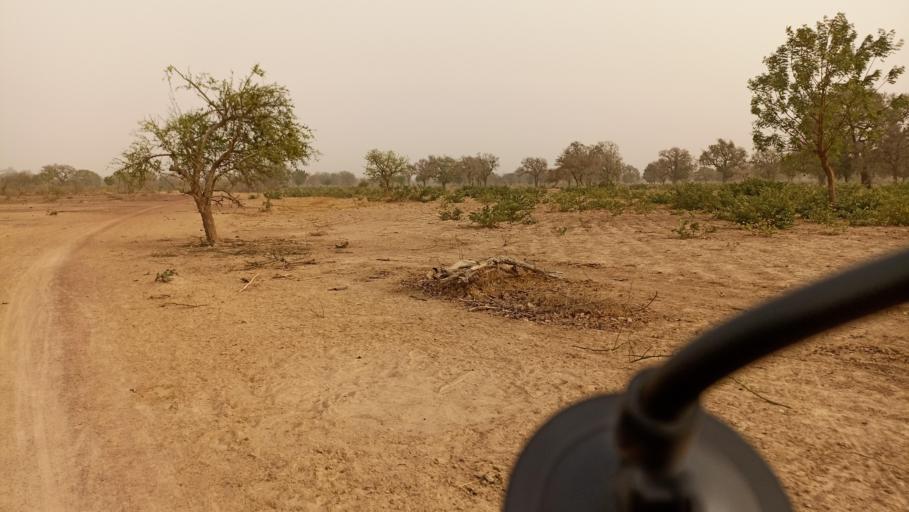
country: BF
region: Boucle du Mouhoun
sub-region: Province du Nayala
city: Toma
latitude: 12.8717
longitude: -2.7554
